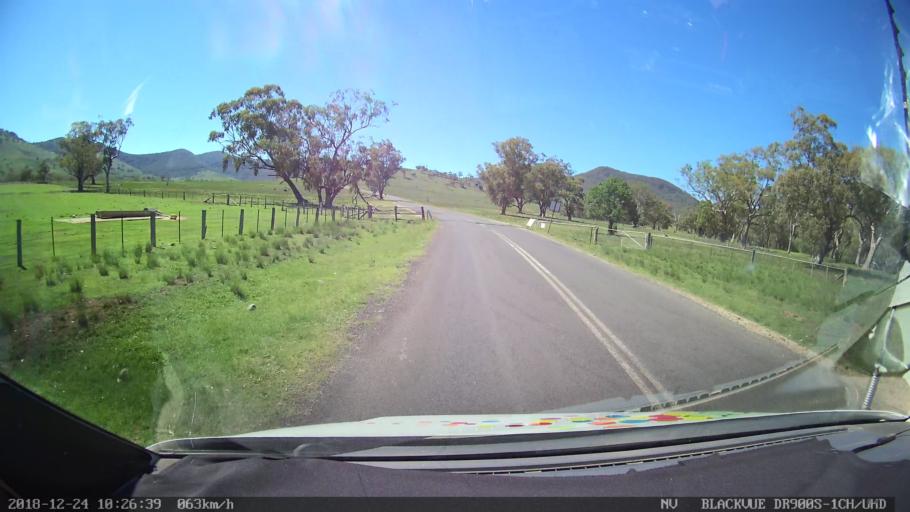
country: AU
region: New South Wales
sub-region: Liverpool Plains
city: Quirindi
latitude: -31.8113
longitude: 150.5272
